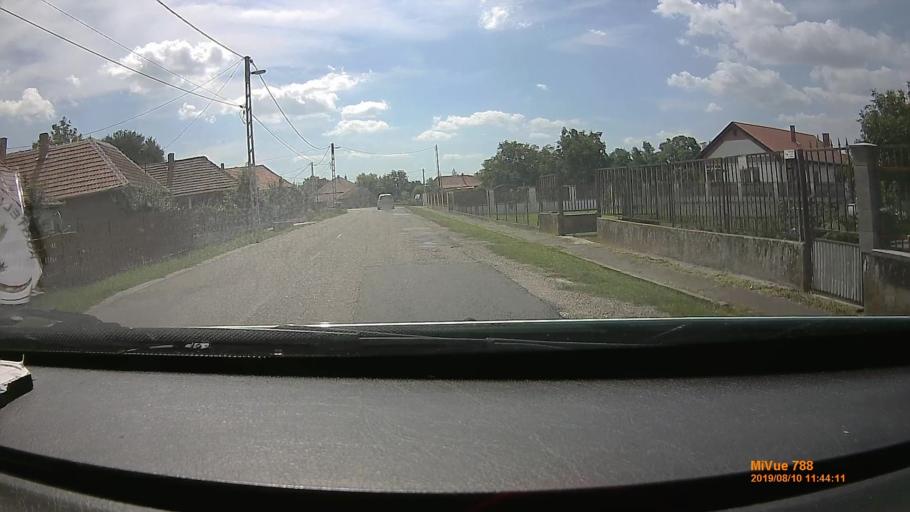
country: HU
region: Borsod-Abauj-Zemplen
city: Szentistvan
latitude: 47.7226
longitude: 20.6204
